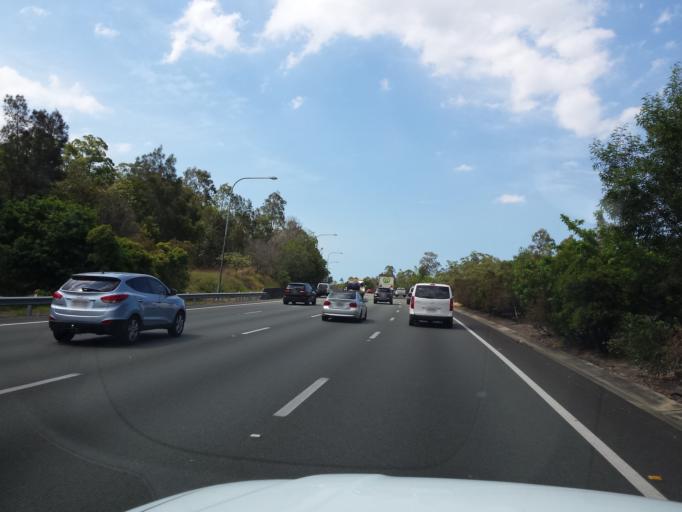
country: AU
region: Queensland
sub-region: Gold Coast
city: Nerang
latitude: -27.9758
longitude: 153.3452
